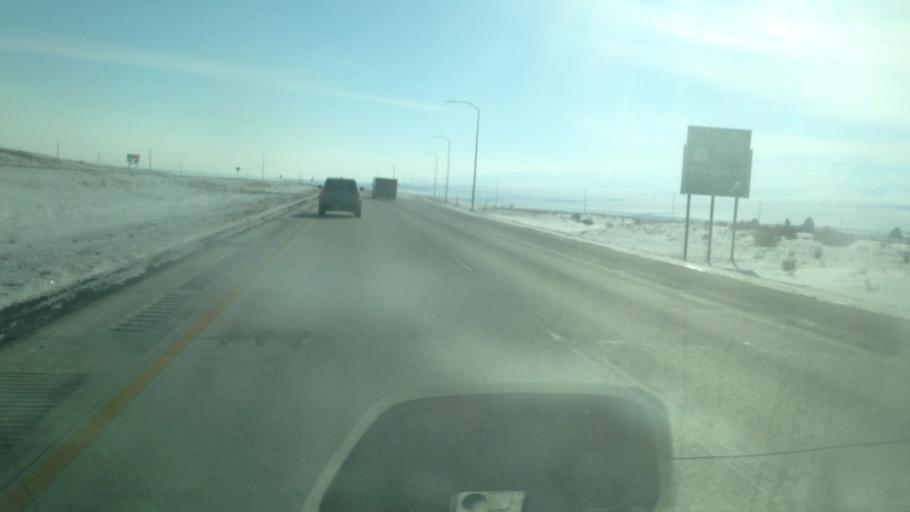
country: US
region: Utah
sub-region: Box Elder County
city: Garland
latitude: 41.8930
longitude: -112.1708
